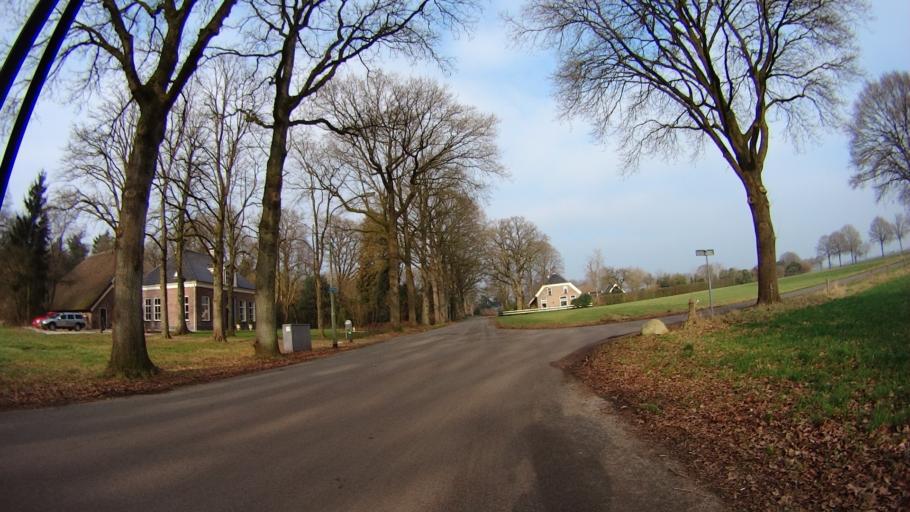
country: NL
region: Drenthe
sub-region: Gemeente Coevorden
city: Sleen
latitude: 52.7489
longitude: 6.8136
